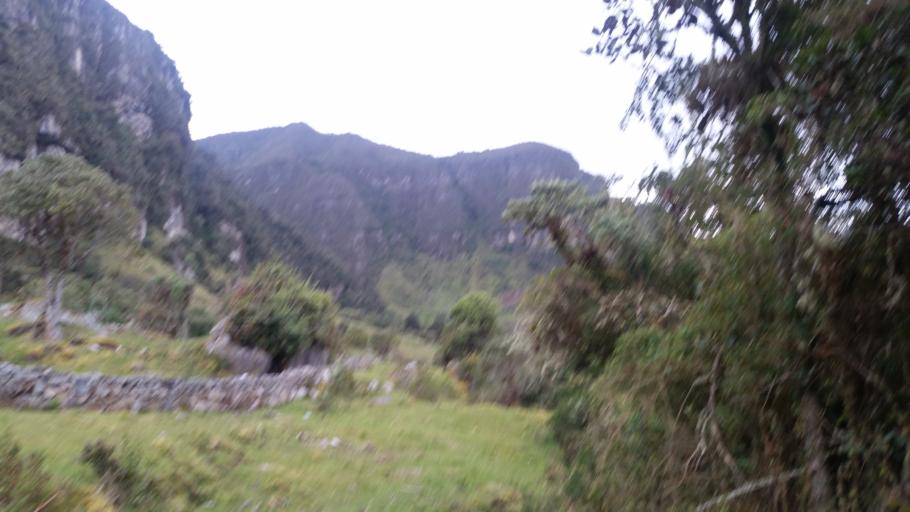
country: CO
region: Cundinamarca
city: Choachi
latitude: 4.5536
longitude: -73.9689
